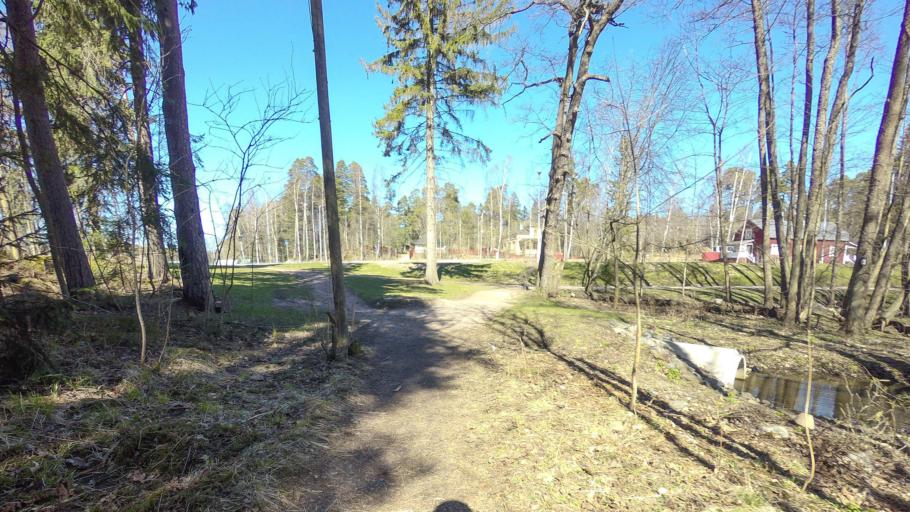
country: FI
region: Uusimaa
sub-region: Helsinki
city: Helsinki
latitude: 60.1686
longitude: 25.0273
